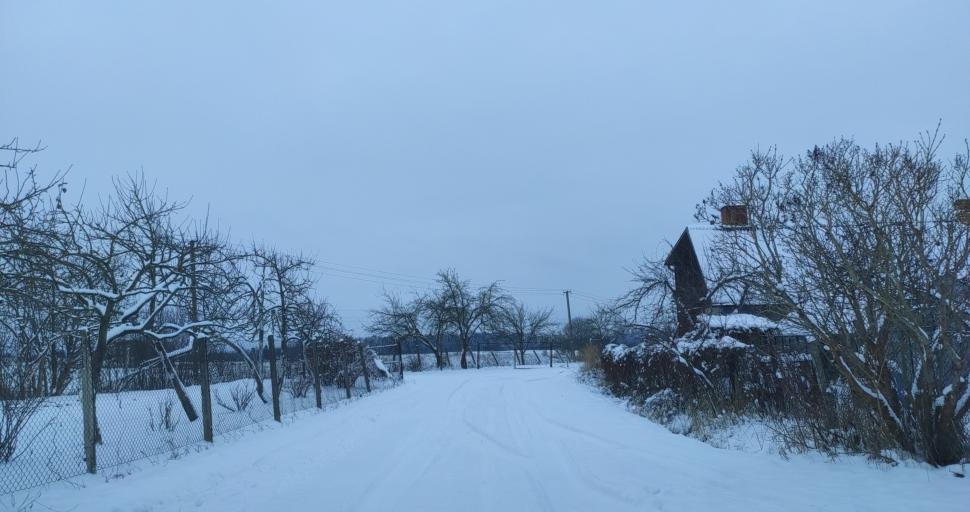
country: LV
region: Kuldigas Rajons
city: Kuldiga
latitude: 56.9505
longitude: 21.9805
